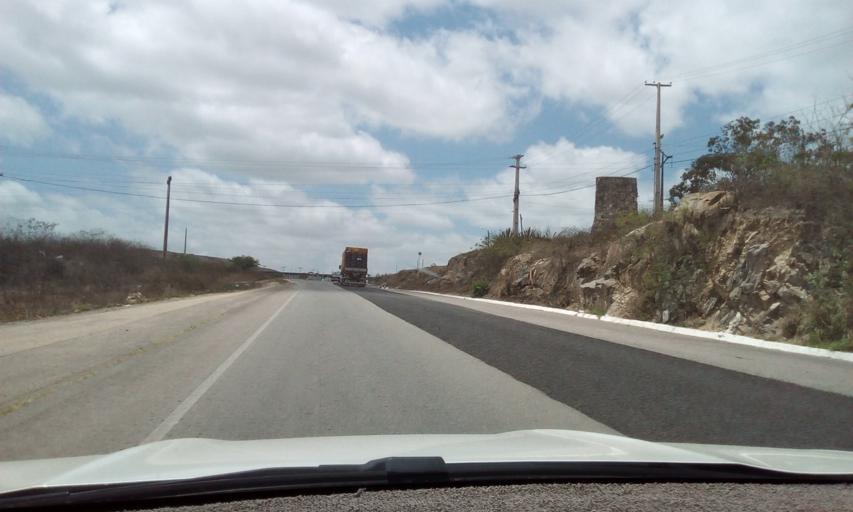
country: BR
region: Pernambuco
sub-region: Caruaru
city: Caruaru
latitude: -8.3019
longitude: -35.9887
